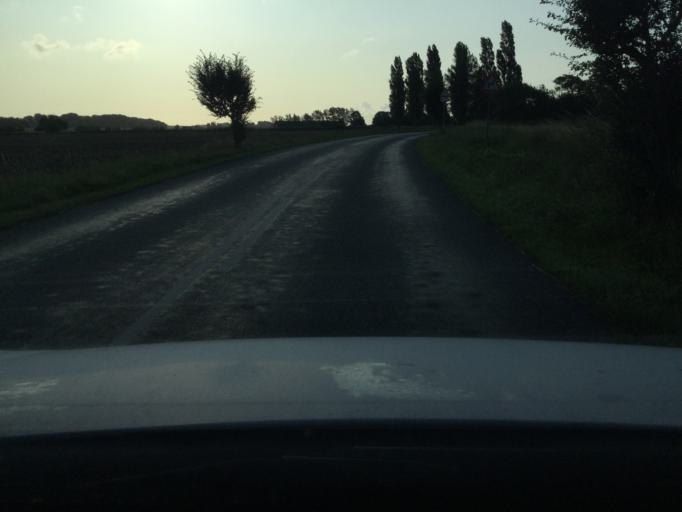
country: DK
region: Zealand
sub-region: Lolland Kommune
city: Rodby
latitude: 54.7123
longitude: 11.3828
